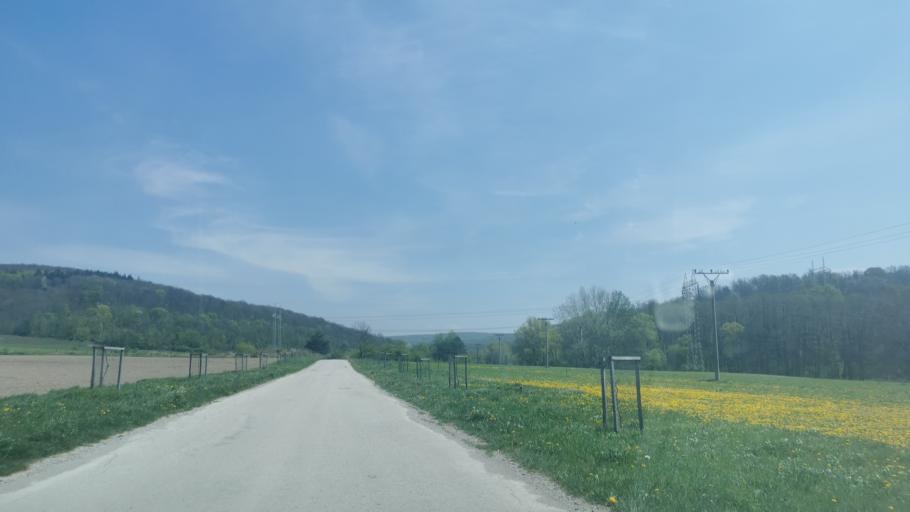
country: SK
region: Trnavsky
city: Smolenice
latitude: 48.5985
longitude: 17.4373
